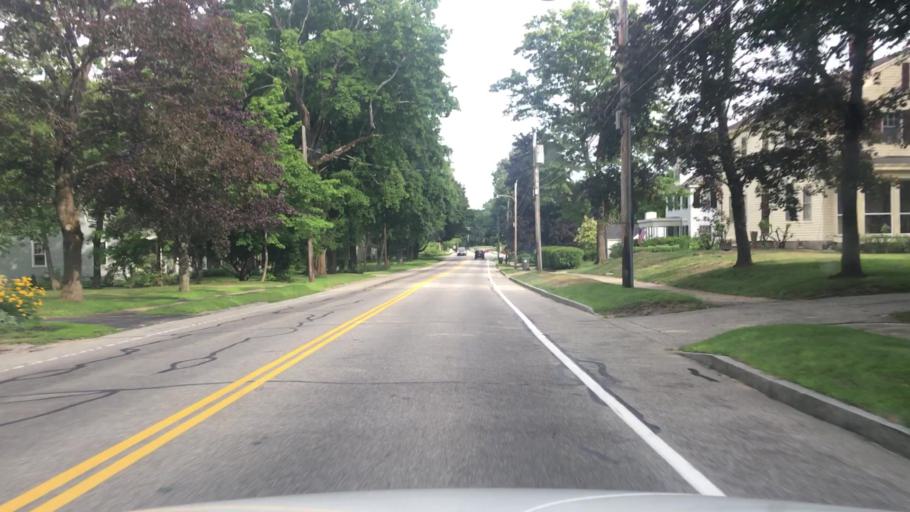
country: US
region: Maine
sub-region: York County
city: Kennebunk
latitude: 43.3847
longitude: -70.5303
